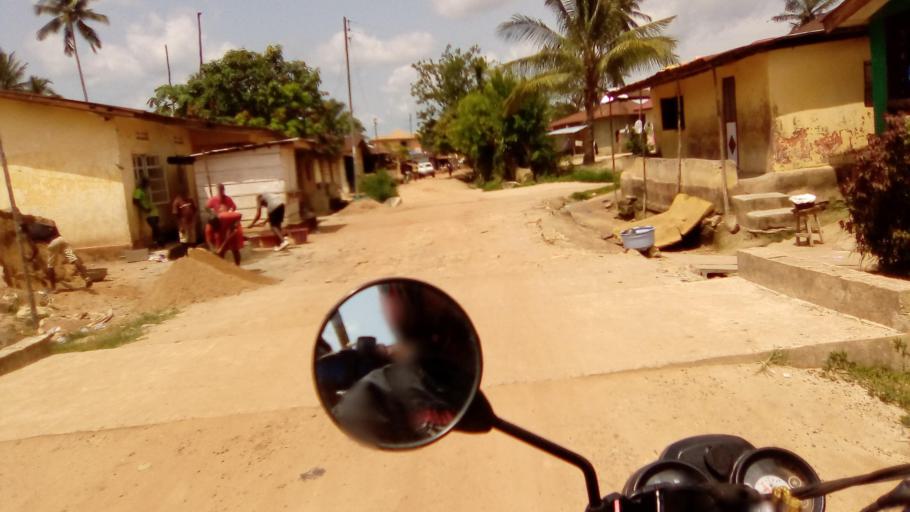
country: SL
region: Southern Province
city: Bo
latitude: 7.9640
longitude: -11.7316
